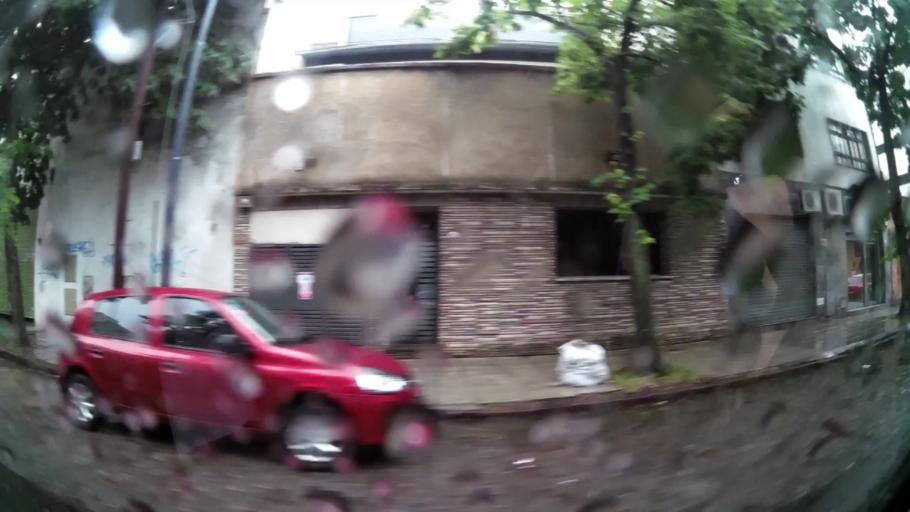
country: AR
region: Buenos Aires
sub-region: Partido de Avellaneda
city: Avellaneda
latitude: -34.6401
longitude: -58.3721
